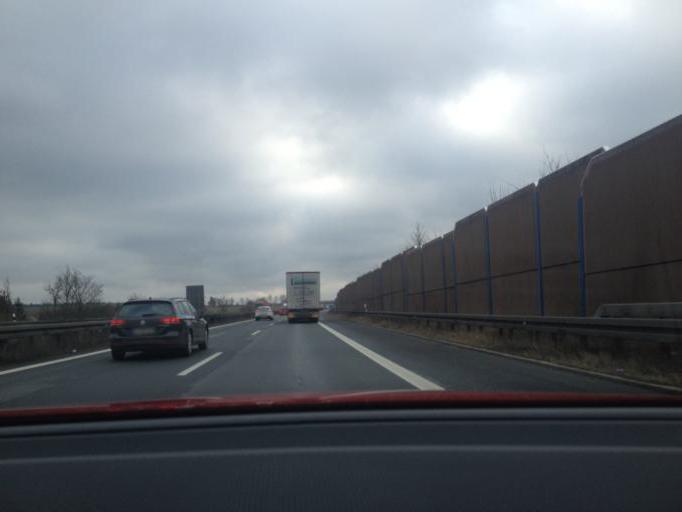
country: DE
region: Bavaria
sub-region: Upper Franconia
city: Rehau
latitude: 50.2517
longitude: 12.0564
